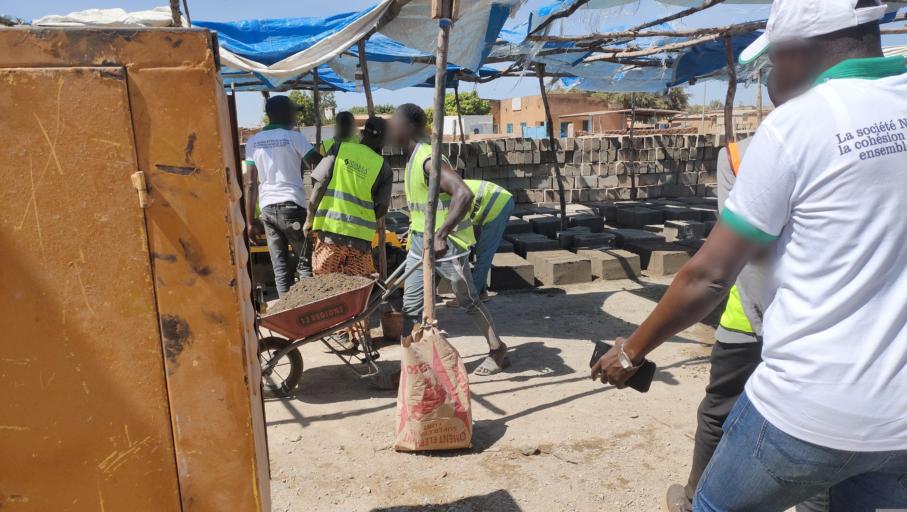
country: BF
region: Est
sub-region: Province du Gourma
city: Fada N'gourma
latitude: 12.0626
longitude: 0.3724
